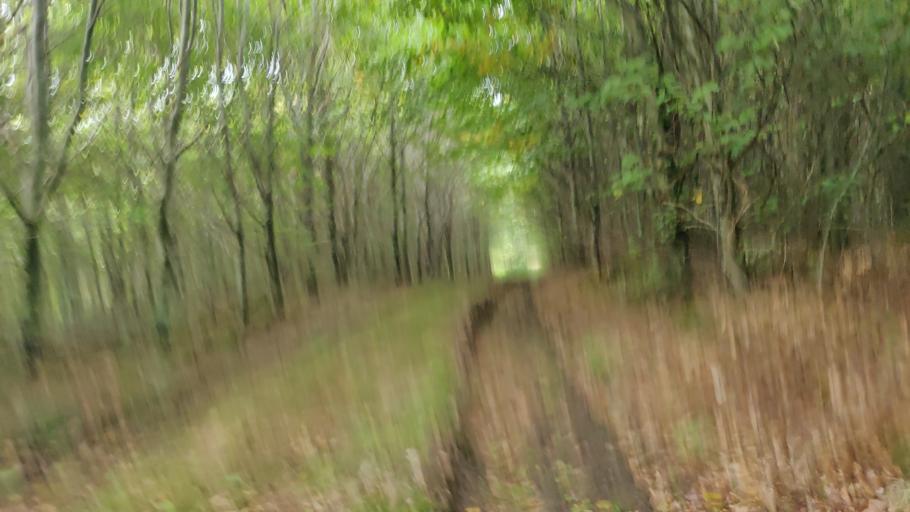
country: DK
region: South Denmark
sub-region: Kolding Kommune
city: Lunderskov
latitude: 55.5465
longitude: 9.3636
